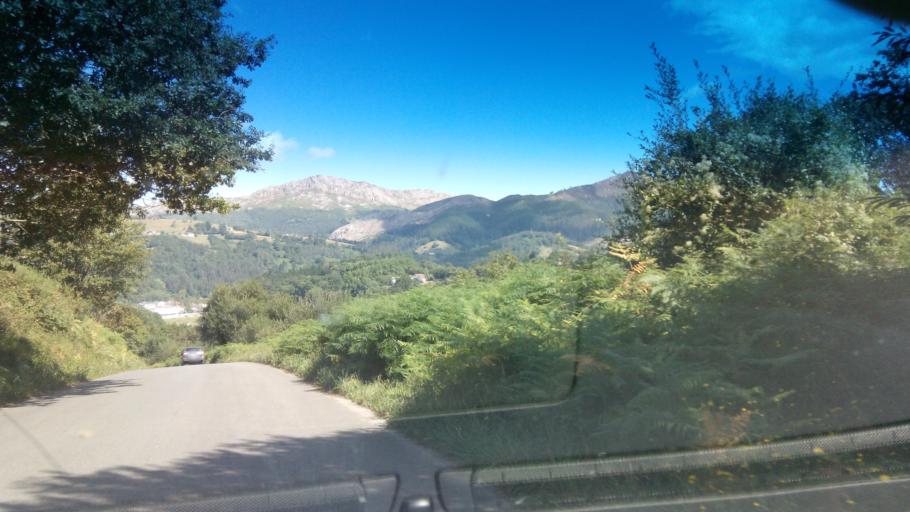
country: ES
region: Asturias
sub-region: Province of Asturias
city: Parres
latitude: 43.3805
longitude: -5.1785
